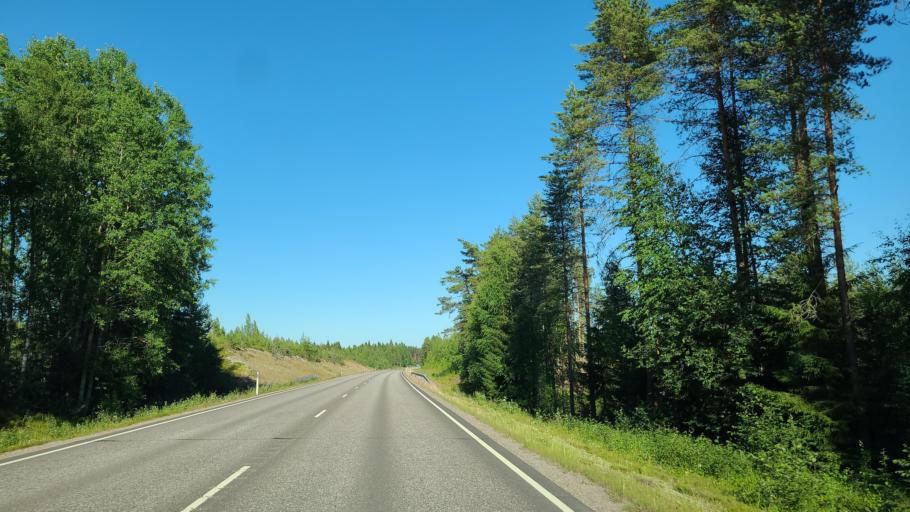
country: FI
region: Southern Savonia
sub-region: Pieksaemaeki
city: Pieksaemaeki
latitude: 62.3331
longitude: 26.8385
